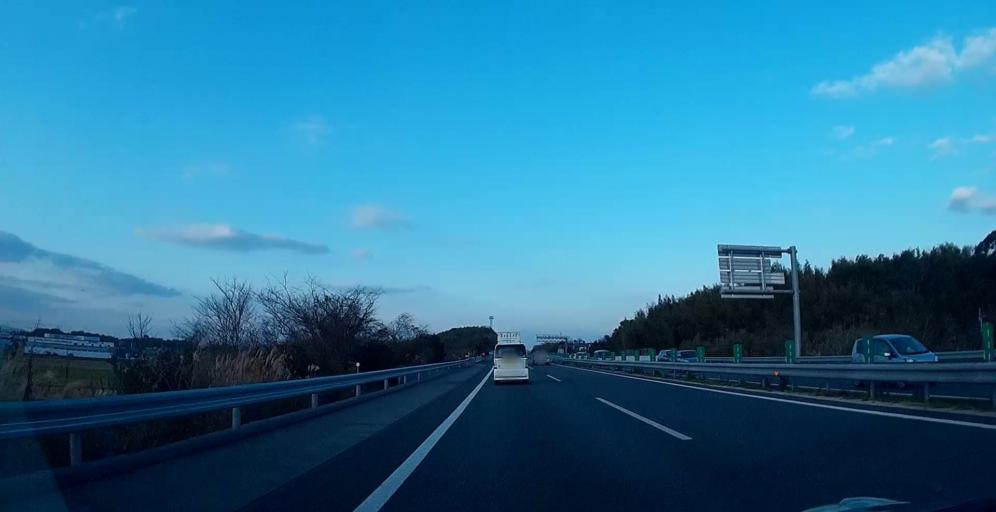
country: JP
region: Kumamoto
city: Uto
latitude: 32.7199
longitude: 130.7701
